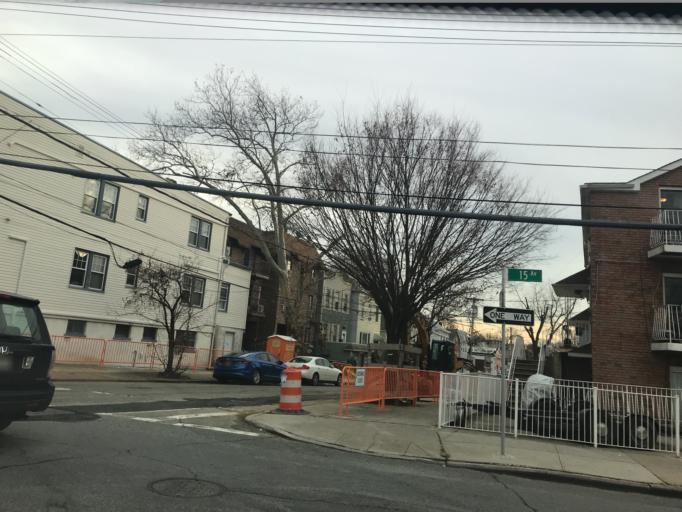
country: US
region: New York
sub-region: Bronx
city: The Bronx
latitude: 40.7846
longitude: -73.8441
